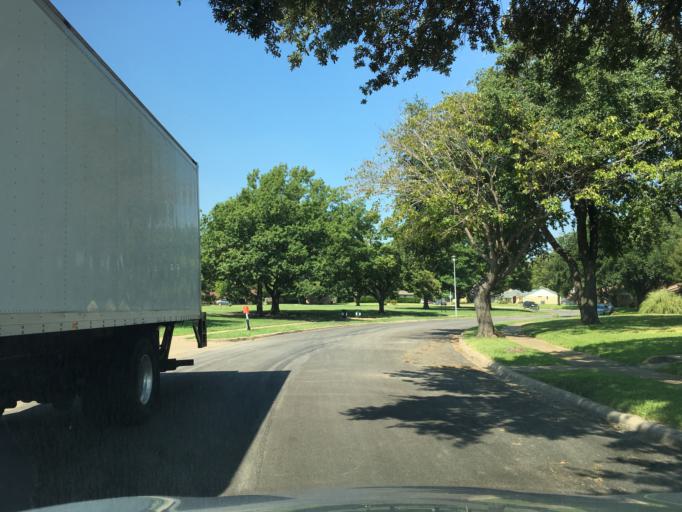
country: US
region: Texas
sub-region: Dallas County
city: Garland
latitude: 32.9326
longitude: -96.6502
